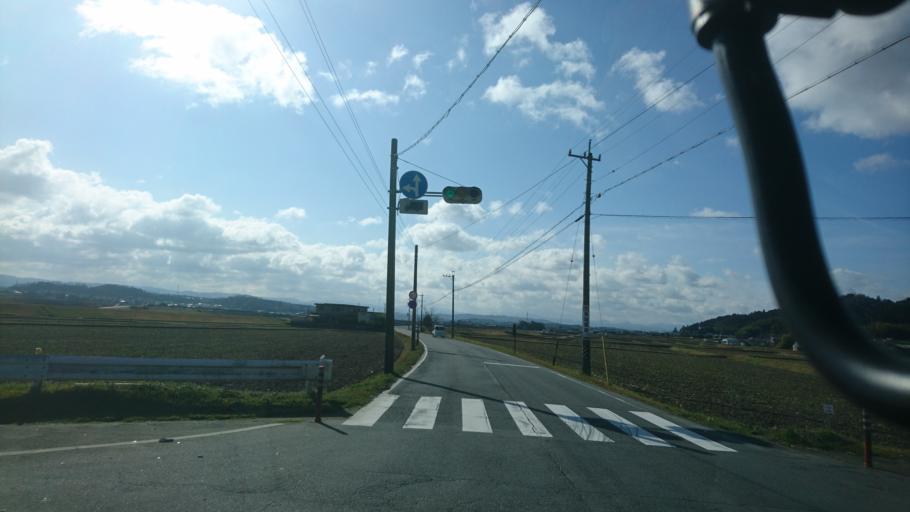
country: JP
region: Mie
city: Ueno-ebisumachi
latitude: 34.7665
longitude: 136.1081
